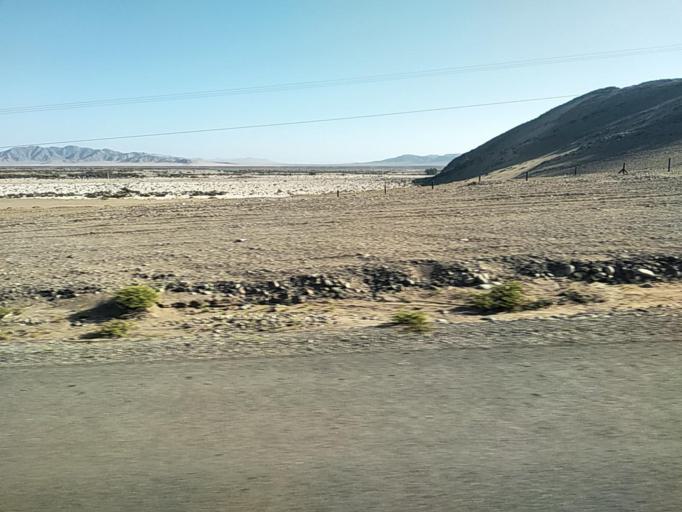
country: CL
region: Atacama
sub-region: Provincia de Copiapo
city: Copiapo
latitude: -27.3513
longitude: -70.6775
